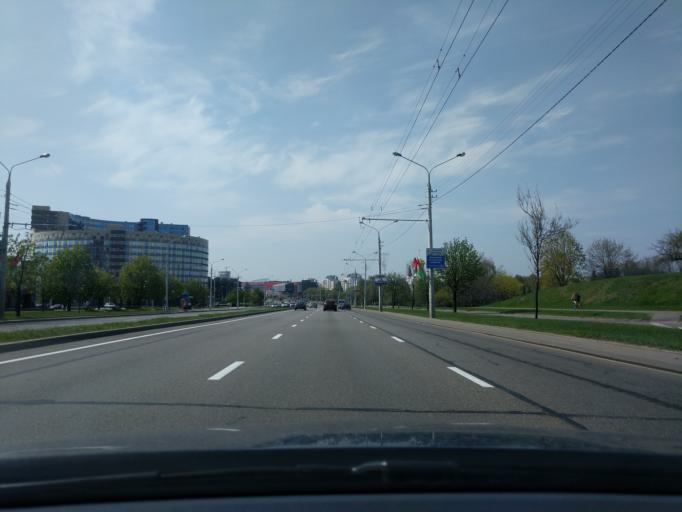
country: BY
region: Minsk
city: Novoye Medvezhino
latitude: 53.9351
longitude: 27.4998
